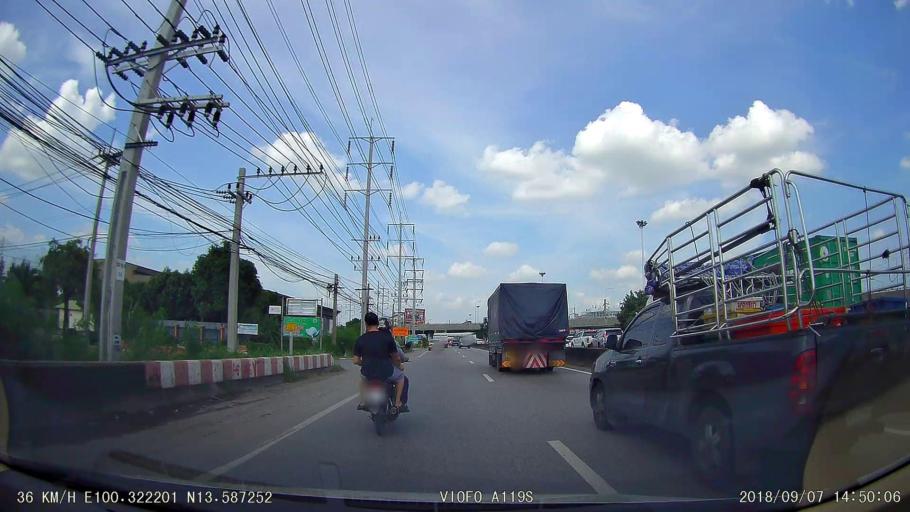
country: TH
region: Samut Sakhon
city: Samut Sakhon
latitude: 13.5877
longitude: 100.3223
